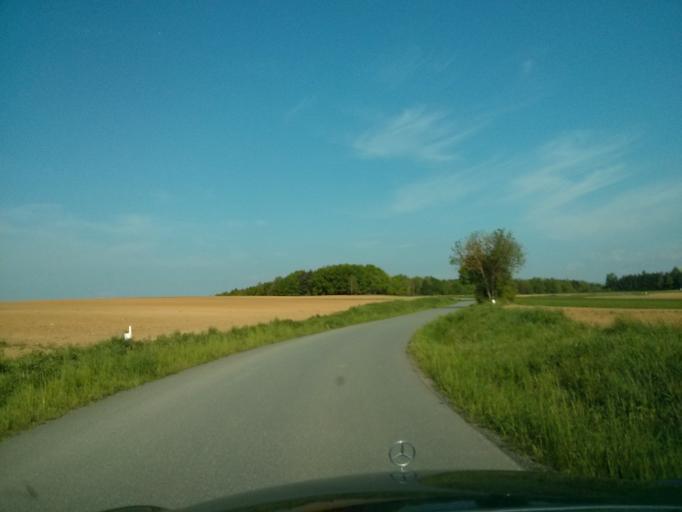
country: AT
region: Burgenland
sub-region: Politischer Bezirk Oberwart
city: Bad Tatzmannsdorf
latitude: 47.3214
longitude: 16.1879
